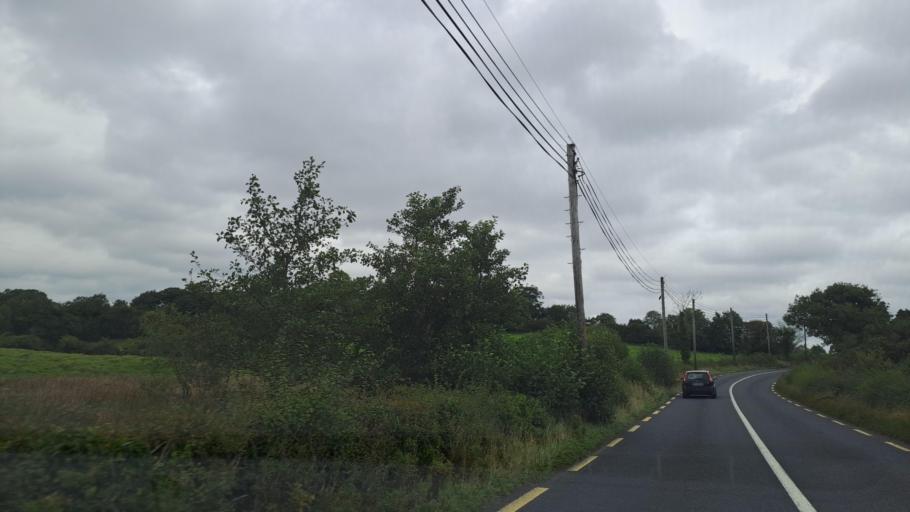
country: IE
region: Ulster
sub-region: An Cabhan
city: Bailieborough
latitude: 53.9875
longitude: -6.9105
